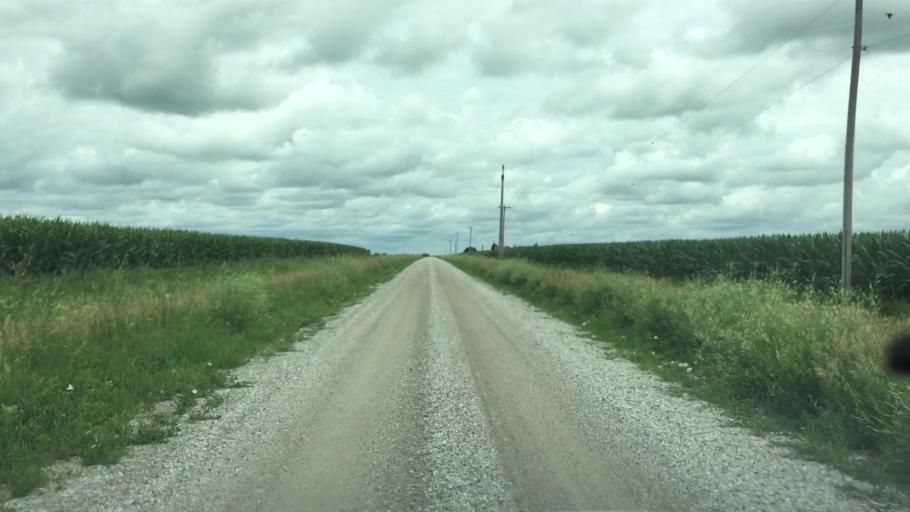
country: US
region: Iowa
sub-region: Jasper County
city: Monroe
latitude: 41.5720
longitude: -93.1208
